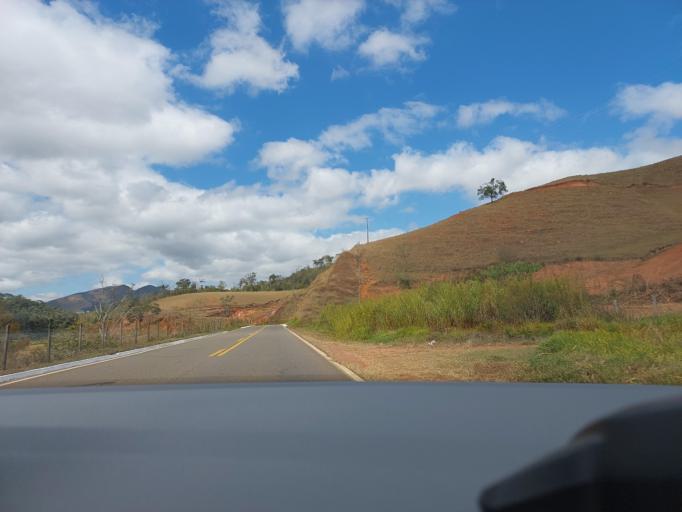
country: BR
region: Minas Gerais
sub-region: Visconde Do Rio Branco
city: Visconde do Rio Branco
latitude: -20.9337
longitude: -42.6323
